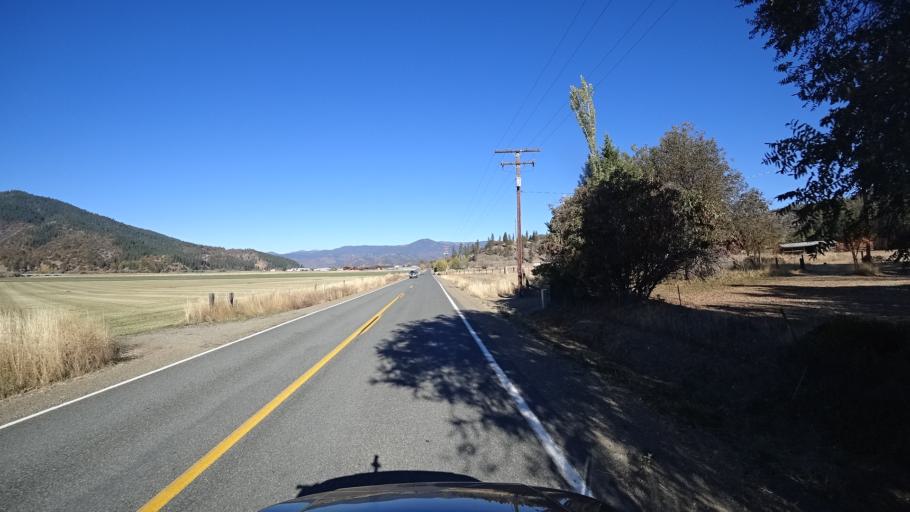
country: US
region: California
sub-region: Siskiyou County
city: Yreka
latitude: 41.5950
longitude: -122.8415
